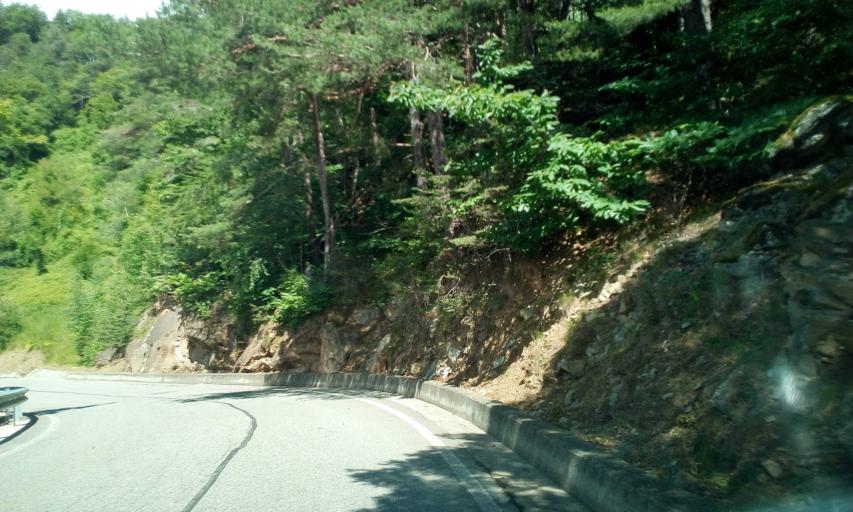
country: IT
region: Aosta Valley
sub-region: Valle d'Aosta
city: Berriat
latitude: 45.7004
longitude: 7.6891
